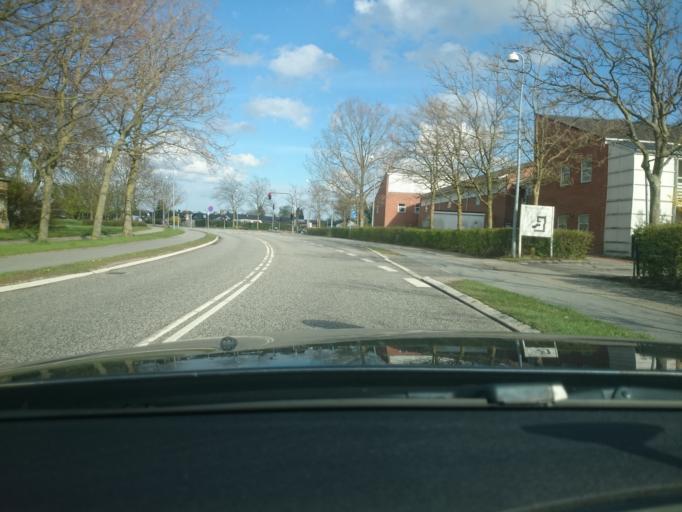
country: DK
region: Capital Region
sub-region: Fureso Kommune
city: Vaerlose
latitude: 55.7850
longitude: 12.3749
